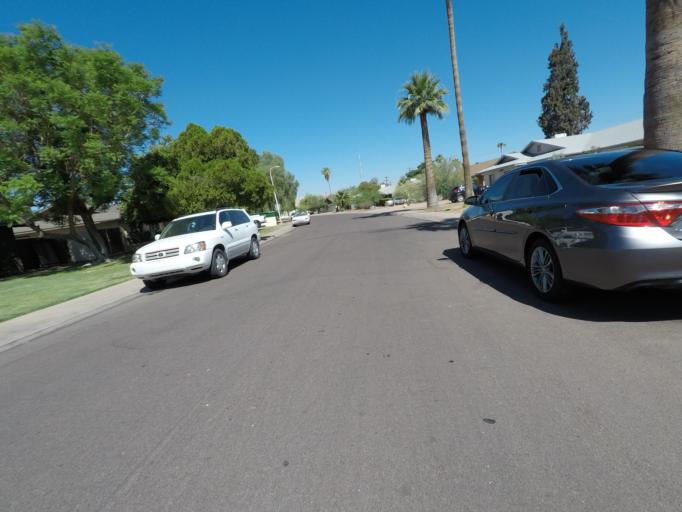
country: US
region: Arizona
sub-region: Maricopa County
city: Tempe Junction
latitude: 33.3983
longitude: -111.9413
